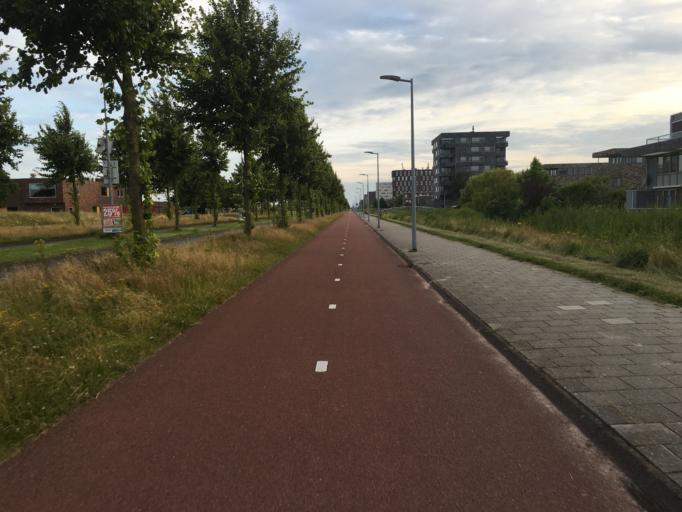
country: NL
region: North Holland
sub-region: Gemeente Heemstede
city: Heemstede
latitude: 52.3161
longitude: 4.6464
